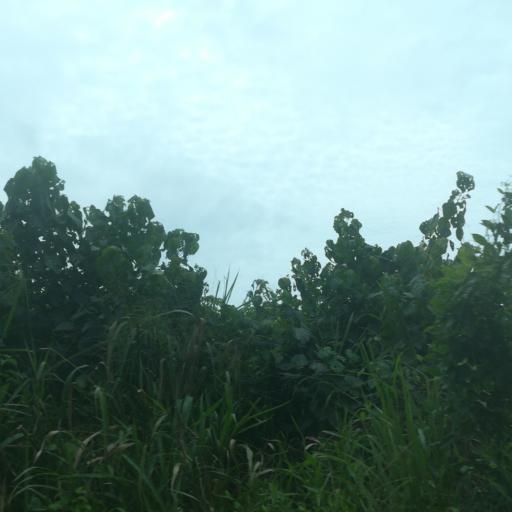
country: NG
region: Lagos
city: Ejirin
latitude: 6.6601
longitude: 3.7262
